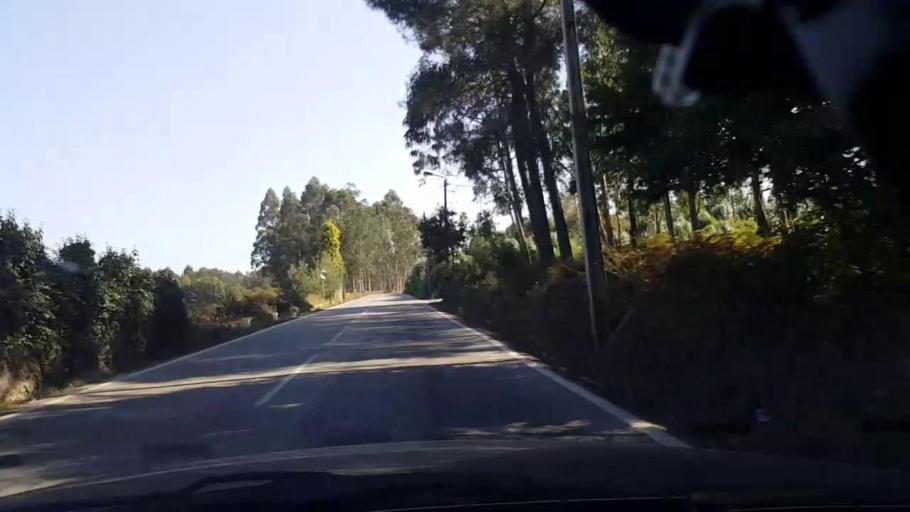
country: PT
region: Porto
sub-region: Vila do Conde
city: Arvore
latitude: 41.3584
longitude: -8.6791
